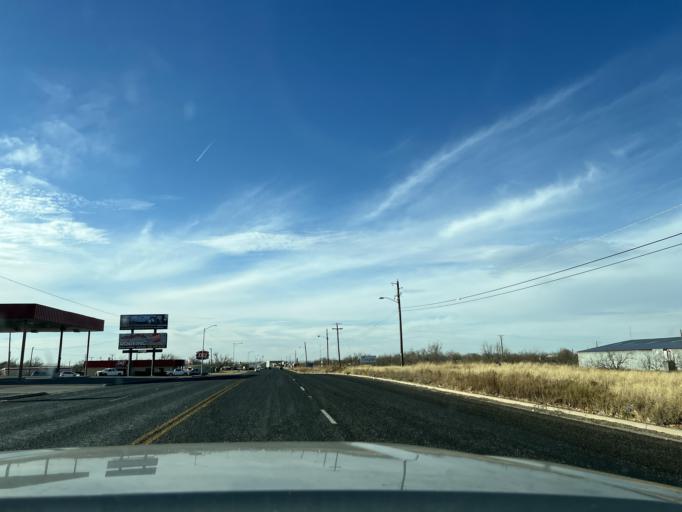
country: US
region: Texas
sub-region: Scurry County
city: Snyder
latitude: 32.7121
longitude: -100.8921
